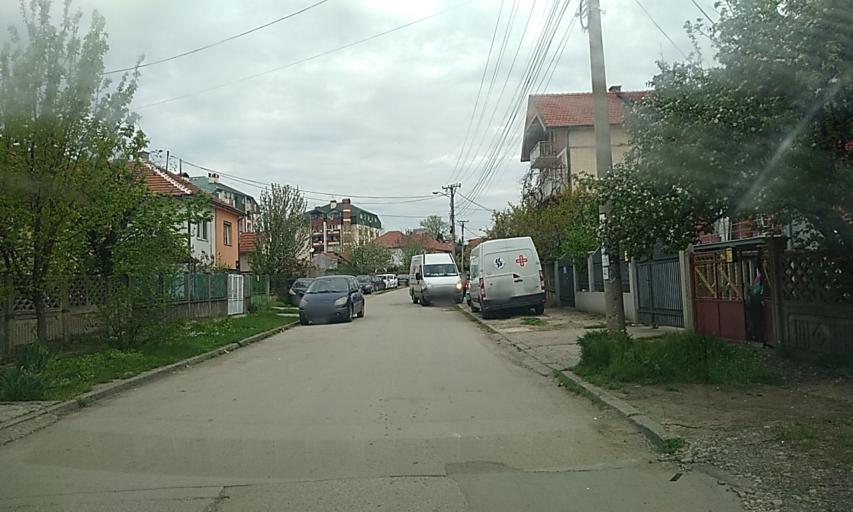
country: RS
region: Central Serbia
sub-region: Nisavski Okrug
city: Nis
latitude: 43.3306
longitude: 21.9103
